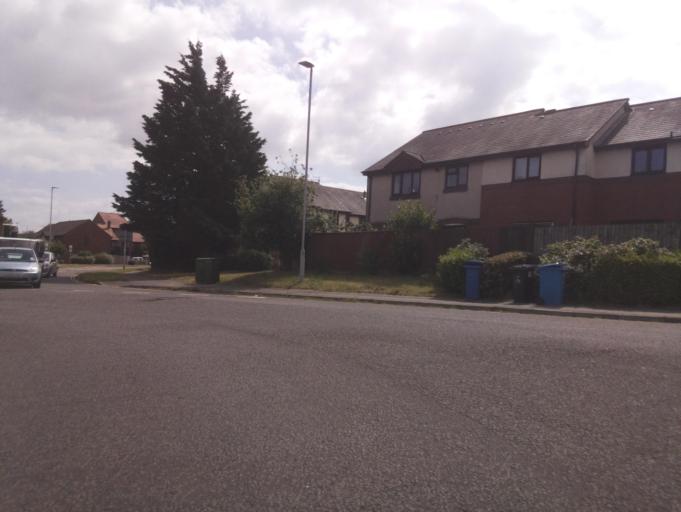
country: GB
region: England
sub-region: Poole
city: Poole
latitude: 50.7136
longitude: -1.9777
